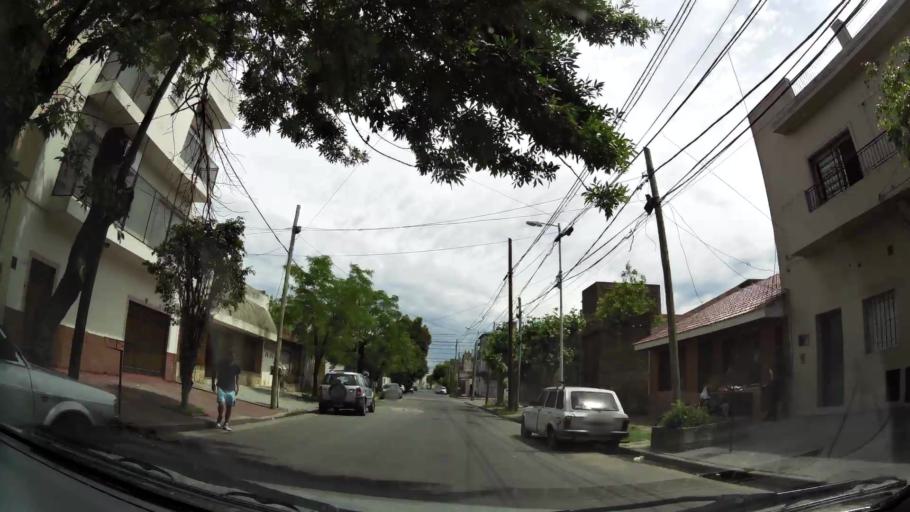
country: AR
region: Buenos Aires
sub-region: Partido de Avellaneda
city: Avellaneda
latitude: -34.6695
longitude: -58.3934
